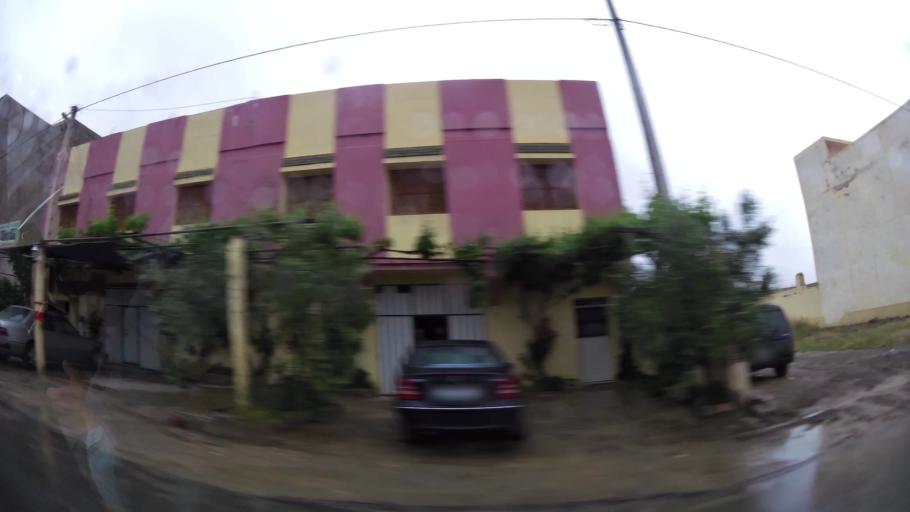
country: MA
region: Taza-Al Hoceima-Taounate
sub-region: Taza
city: Aknoul
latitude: 34.8202
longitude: -3.7265
